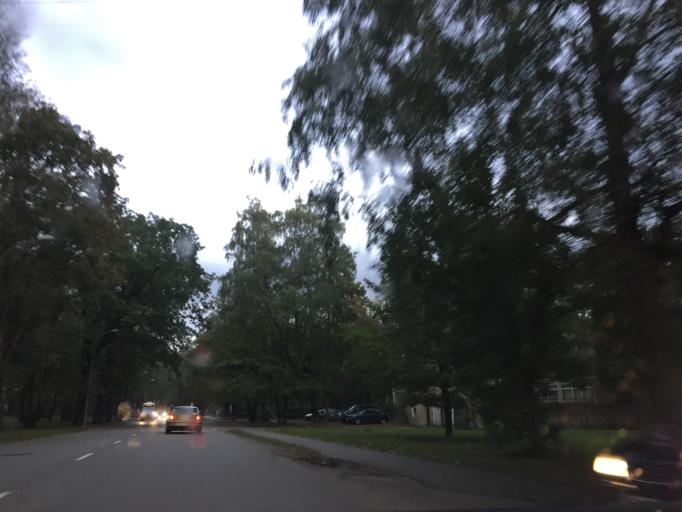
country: LV
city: Tireli
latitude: 56.9569
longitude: 23.6043
